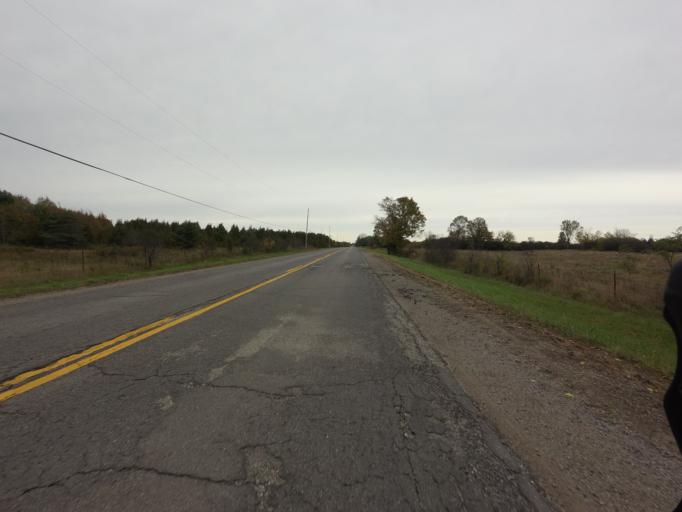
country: CA
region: Ontario
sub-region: Lanark County
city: Smiths Falls
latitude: 44.8751
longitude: -75.8129
